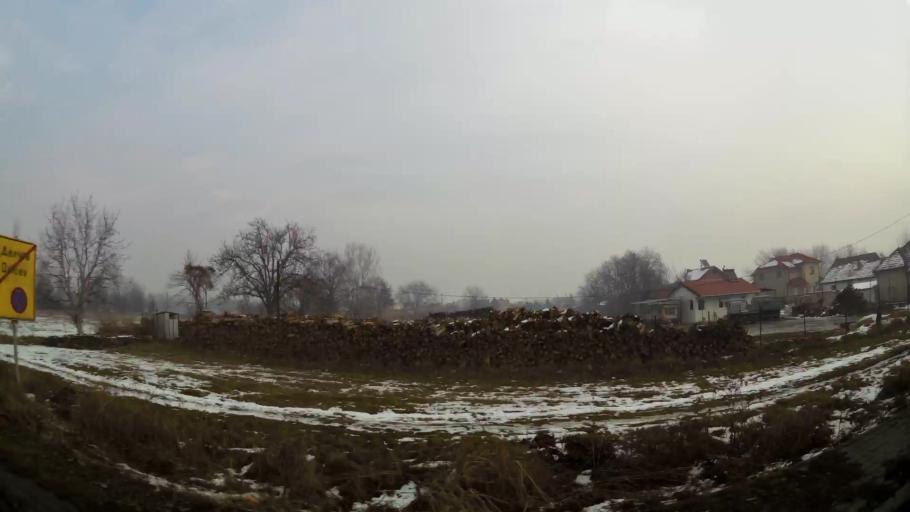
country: MK
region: Ilinden
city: Jurumleri
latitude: 41.9746
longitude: 21.5377
